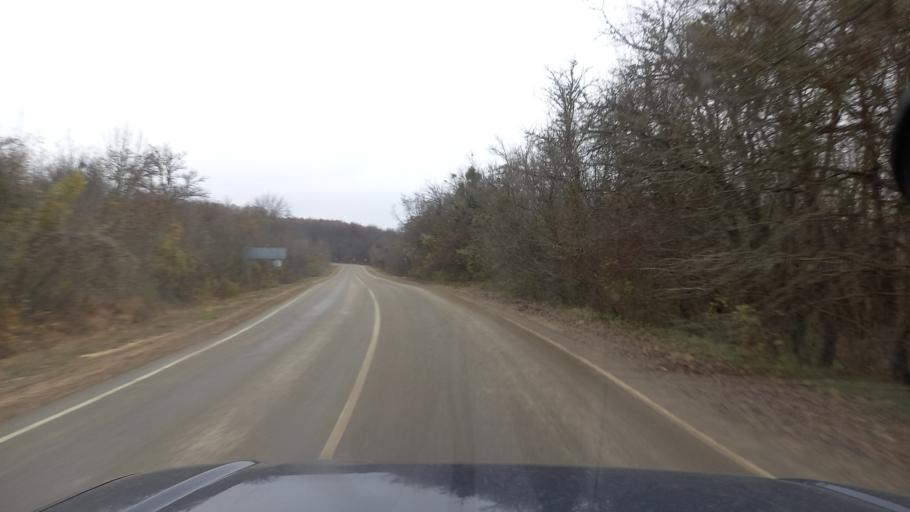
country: RU
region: Krasnodarskiy
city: Goryachiy Klyuch
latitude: 44.5514
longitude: 39.2513
